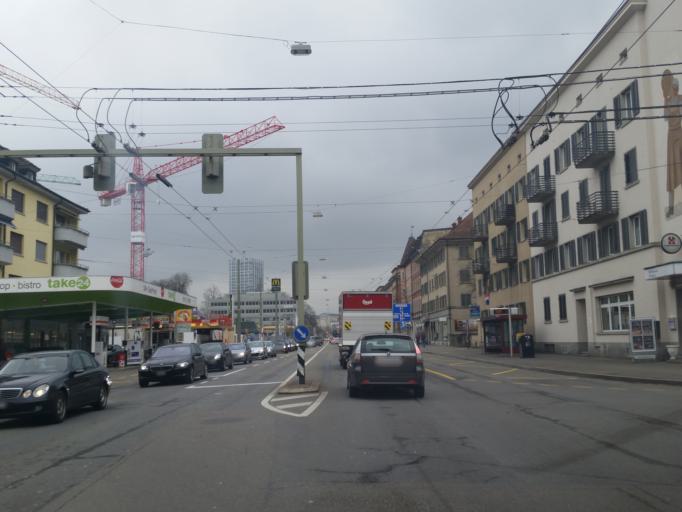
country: CH
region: Zurich
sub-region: Bezirk Winterthur
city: Stadt Winterthur (Kreis 1) / Bruehlberg
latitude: 47.4940
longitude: 8.7106
